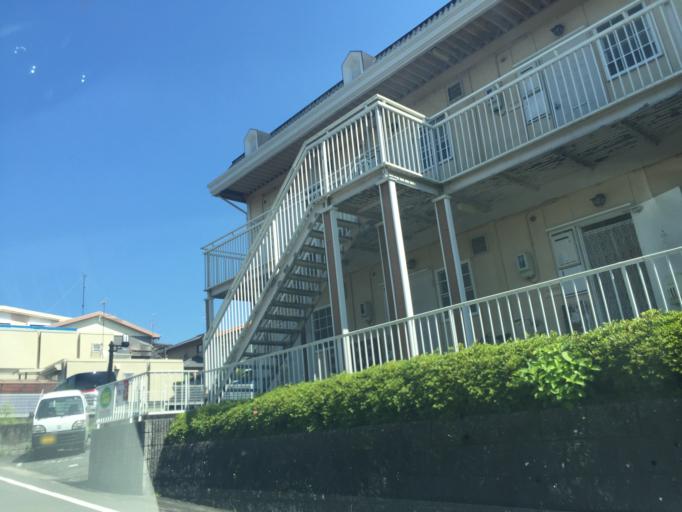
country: JP
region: Shizuoka
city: Kakegawa
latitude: 34.7723
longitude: 137.9980
